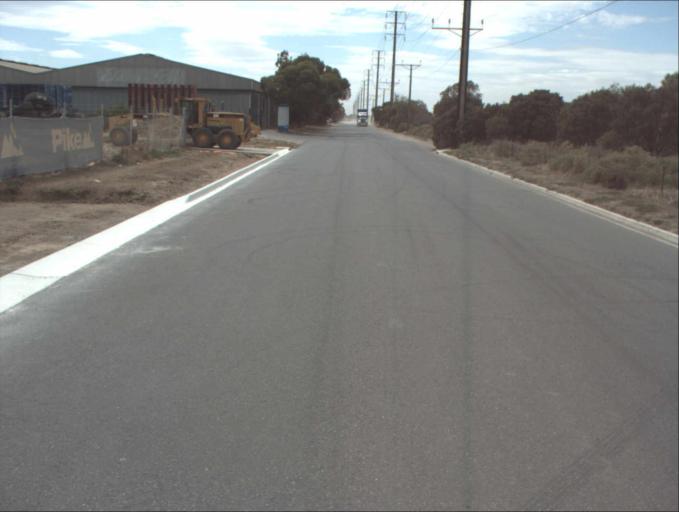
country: AU
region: South Australia
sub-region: Port Adelaide Enfield
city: Birkenhead
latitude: -34.8342
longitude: 138.5198
